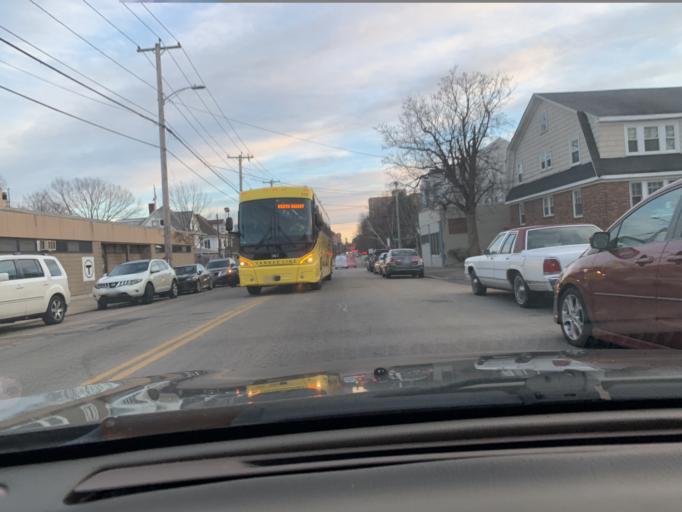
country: US
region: Massachusetts
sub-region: Norfolk County
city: Quincy
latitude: 42.2597
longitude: -71.0099
